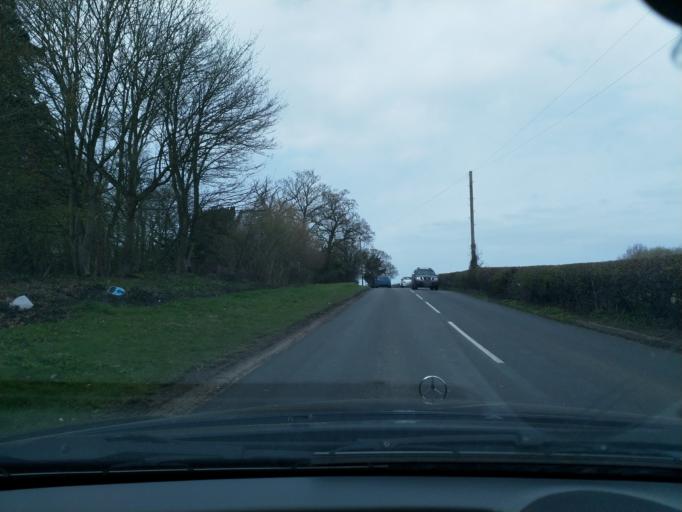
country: GB
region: England
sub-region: Warwickshire
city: Royal Leamington Spa
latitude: 52.3235
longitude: -1.5455
